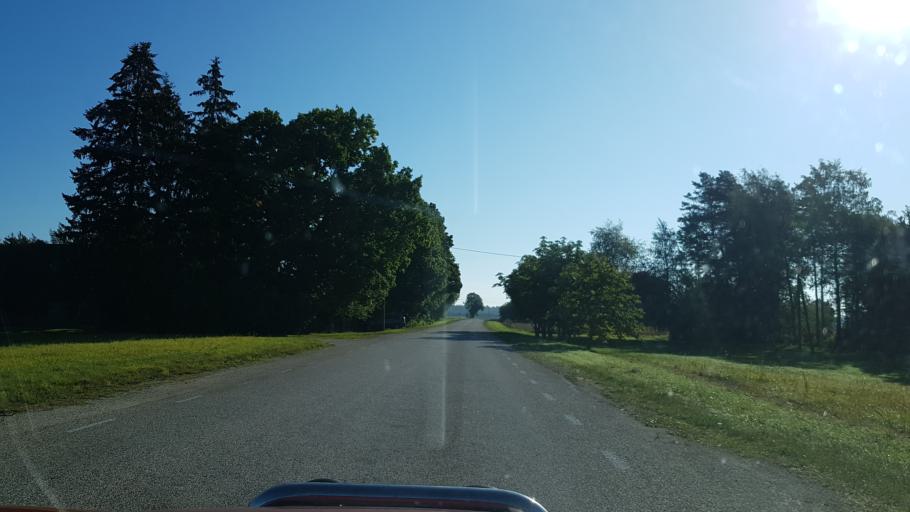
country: EE
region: Jogevamaa
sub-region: Tabivere vald
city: Tabivere
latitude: 58.6820
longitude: 26.6475
